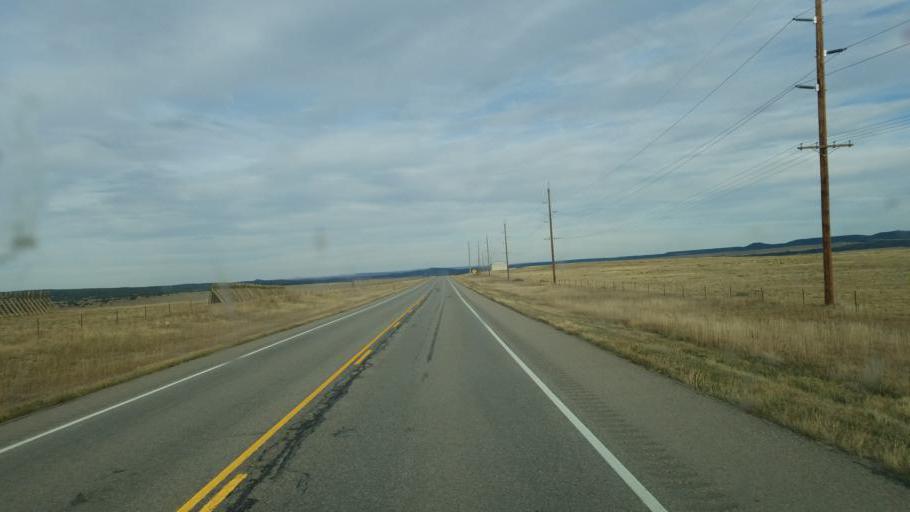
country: US
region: Colorado
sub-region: Huerfano County
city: Walsenburg
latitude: 37.5475
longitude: -104.9916
